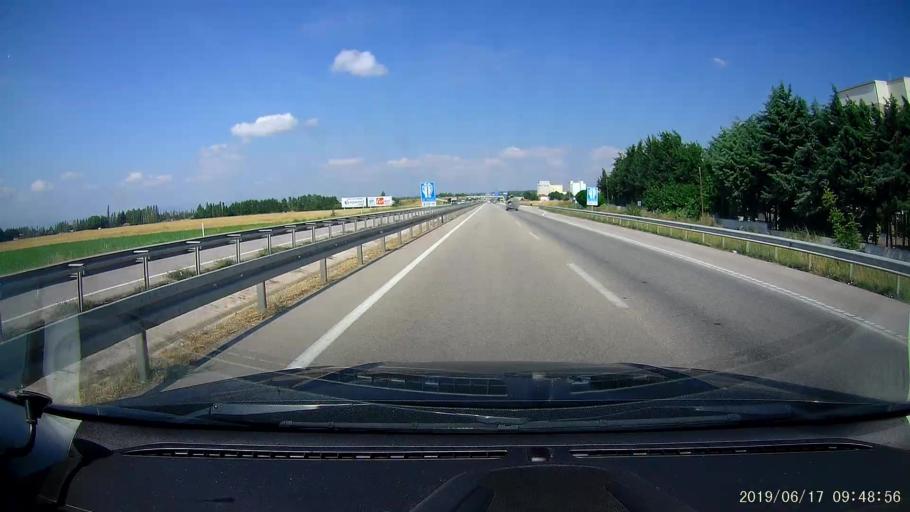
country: TR
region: Amasya
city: Merzifon
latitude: 40.8739
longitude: 35.5402
